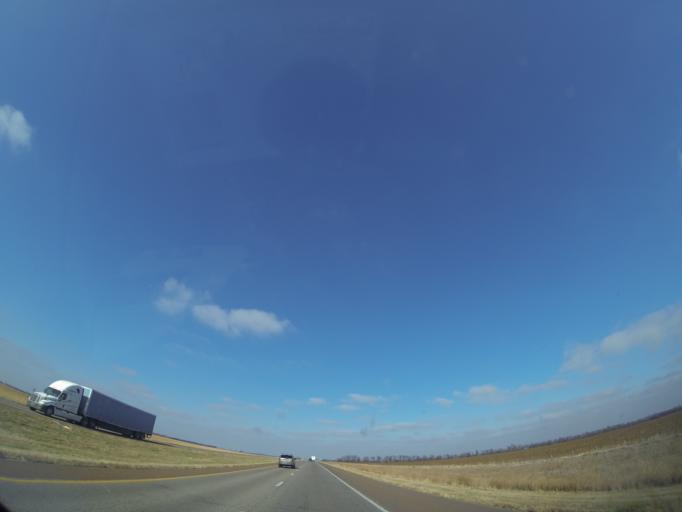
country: US
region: Kansas
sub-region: McPherson County
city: McPherson
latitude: 38.4238
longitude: -97.6206
